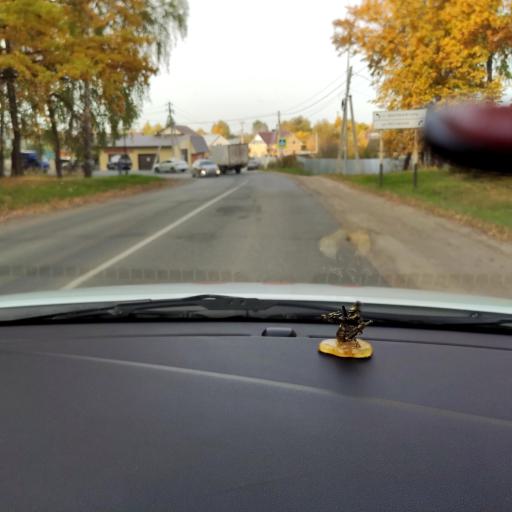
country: RU
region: Tatarstan
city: Vysokaya Gora
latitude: 55.9268
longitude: 49.3036
